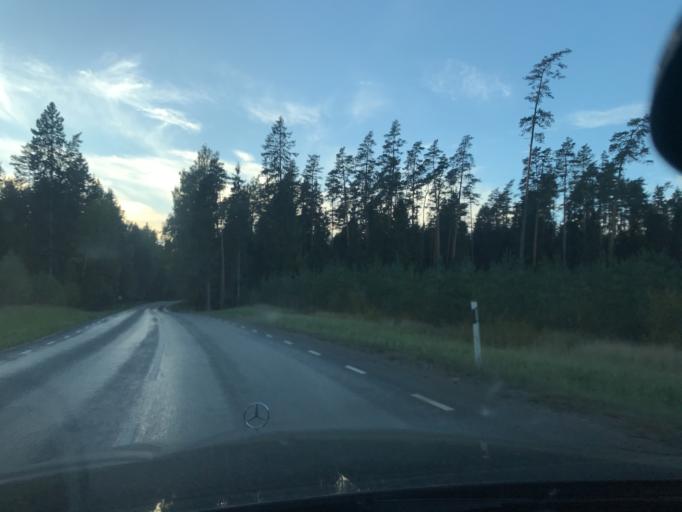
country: EE
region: Vorumaa
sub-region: Antsla vald
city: Vana-Antsla
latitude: 57.8797
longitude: 26.7636
